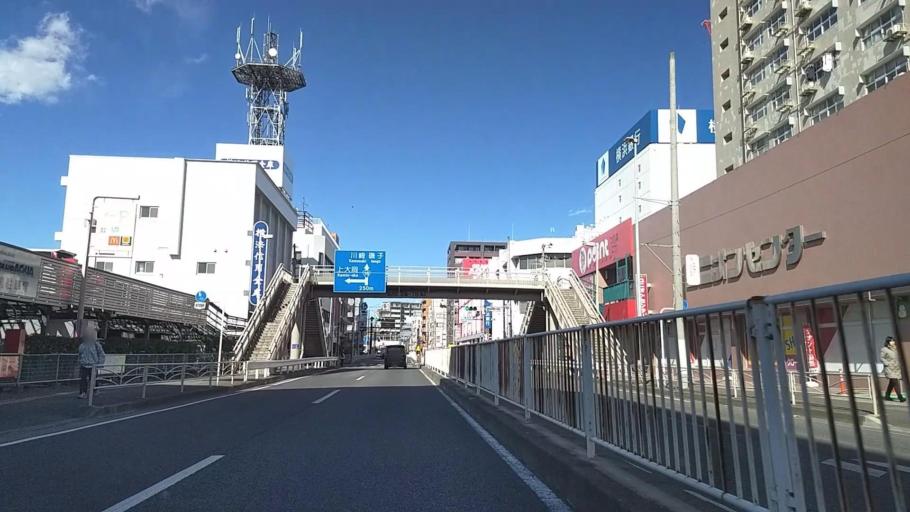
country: JP
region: Kanagawa
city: Zushi
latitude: 35.3385
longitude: 139.6238
